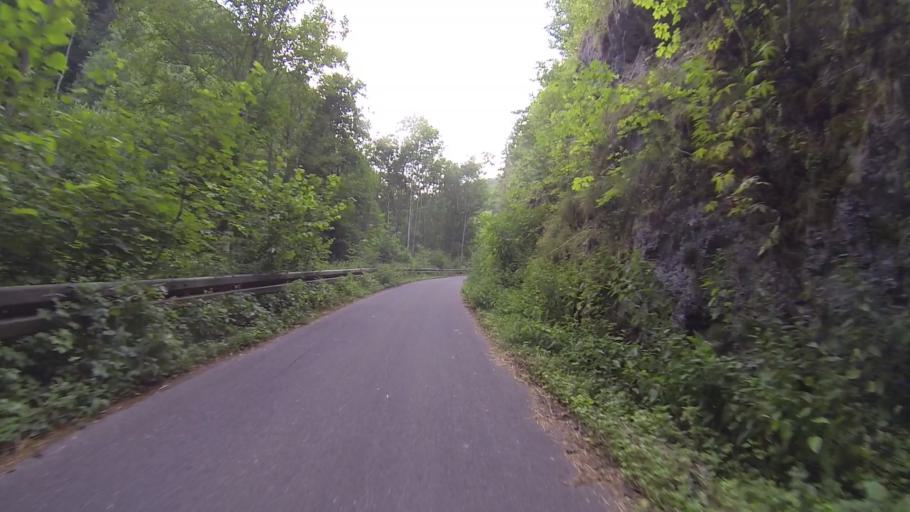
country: DE
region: Baden-Wuerttemberg
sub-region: Tuebingen Region
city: Blaubeuren
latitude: 48.4487
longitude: 9.8535
